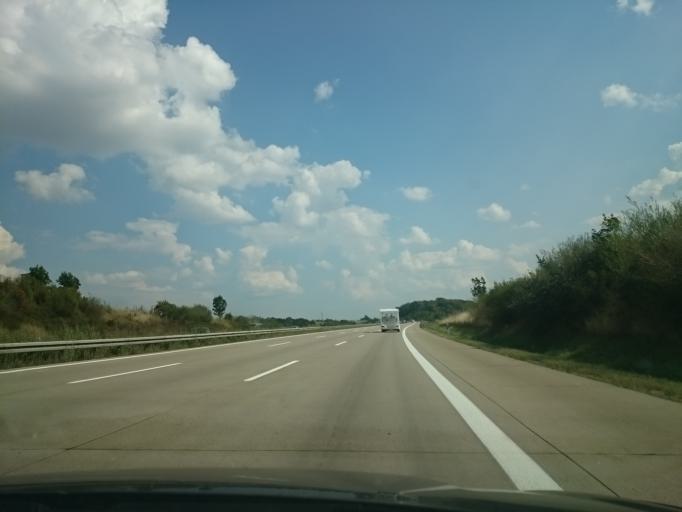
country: DE
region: Saxony
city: Reinsberg
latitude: 51.0601
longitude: 13.4219
